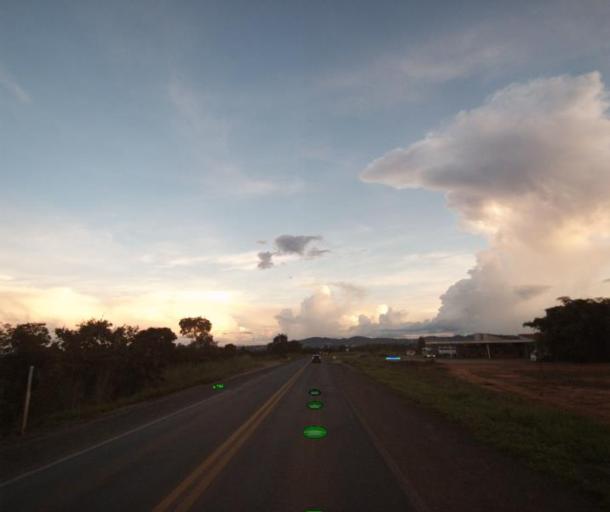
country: BR
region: Goias
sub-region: Uruacu
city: Uruacu
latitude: -14.4752
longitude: -49.1556
